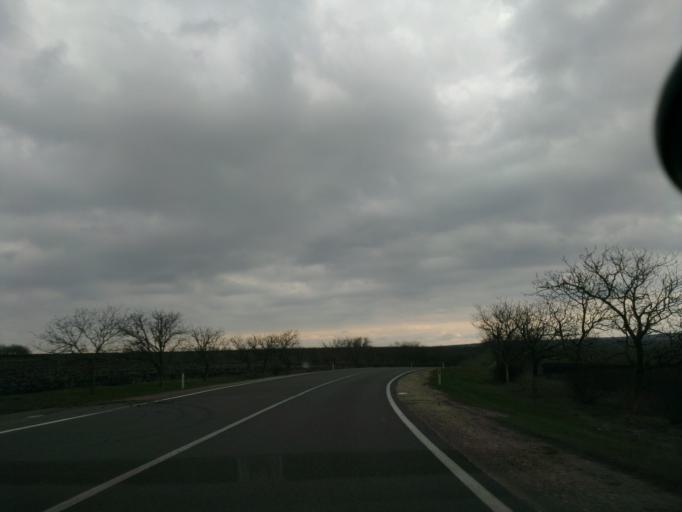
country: MD
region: Gagauzia
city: Bugeac
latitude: 46.4157
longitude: 28.7406
